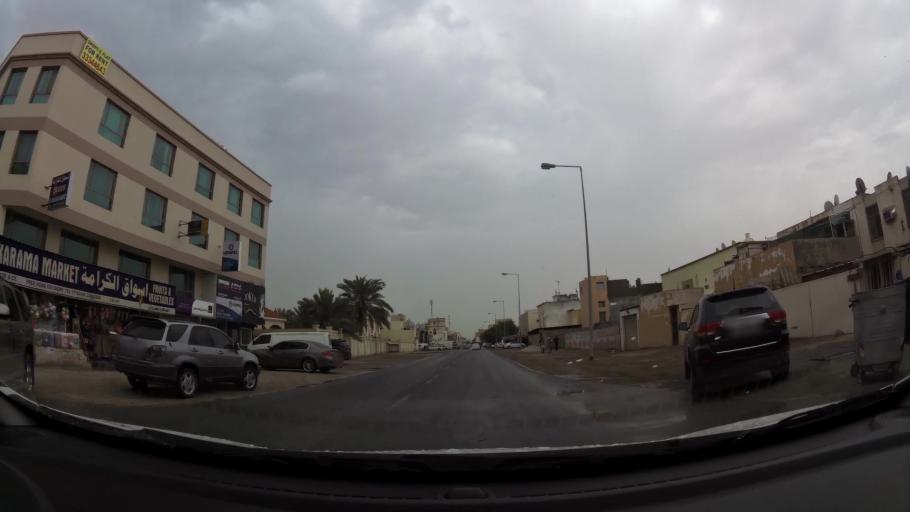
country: BH
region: Northern
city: Madinat `Isa
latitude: 26.1650
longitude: 50.5702
